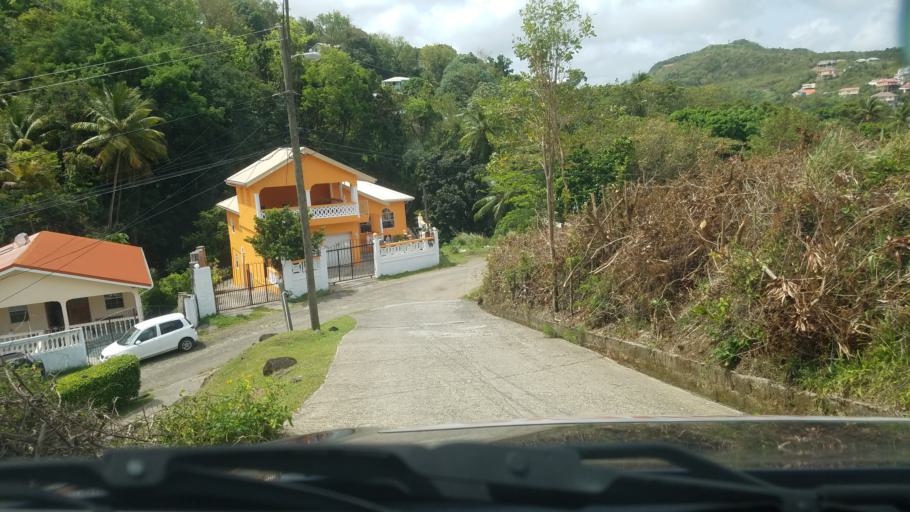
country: LC
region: Gros-Islet
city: Gros Islet
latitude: 14.0463
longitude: -60.9557
